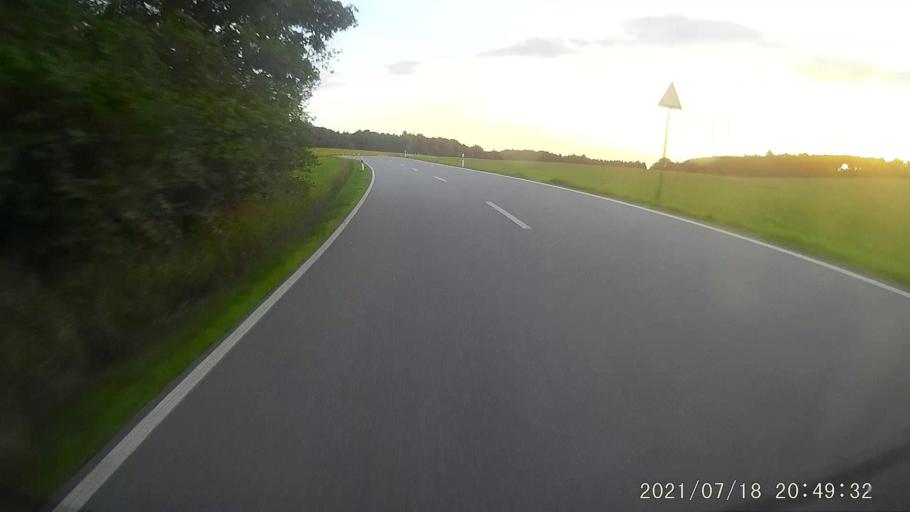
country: DE
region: Saxony
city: Konigshain
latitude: 51.1854
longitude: 14.8320
